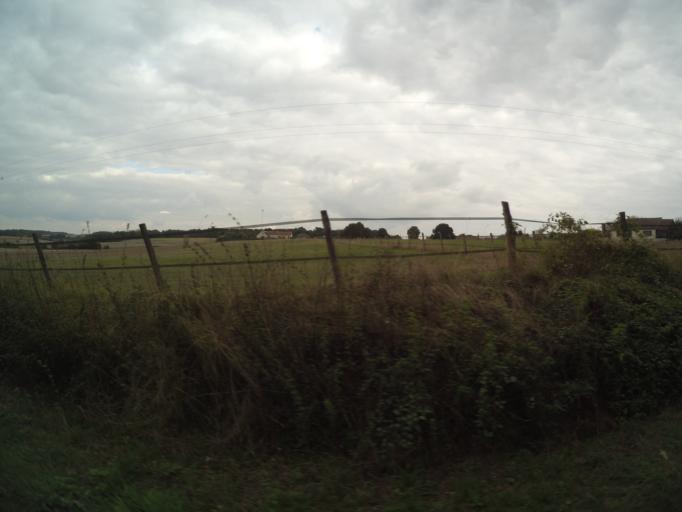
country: FR
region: Centre
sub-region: Departement d'Indre-et-Loire
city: Auzouer-en-Touraine
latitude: 47.4981
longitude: 0.9297
